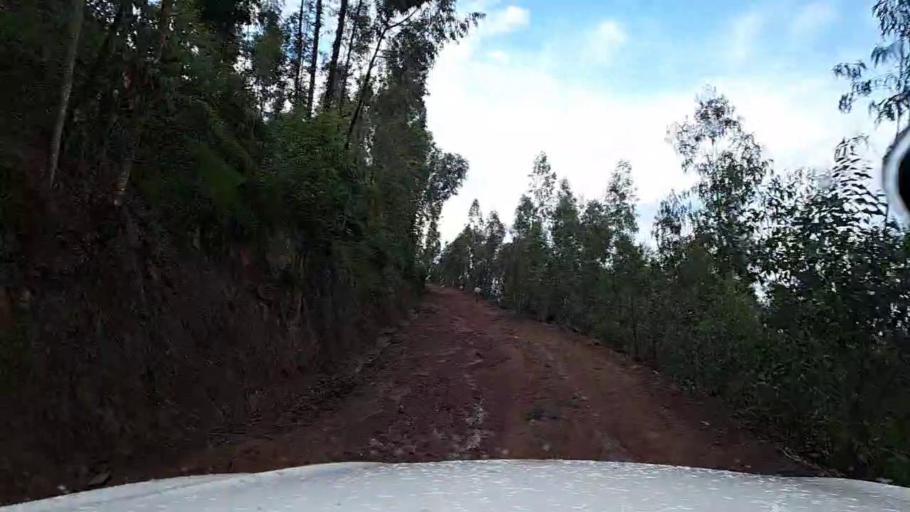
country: RW
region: Northern Province
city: Byumba
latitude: -1.7213
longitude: 29.9116
